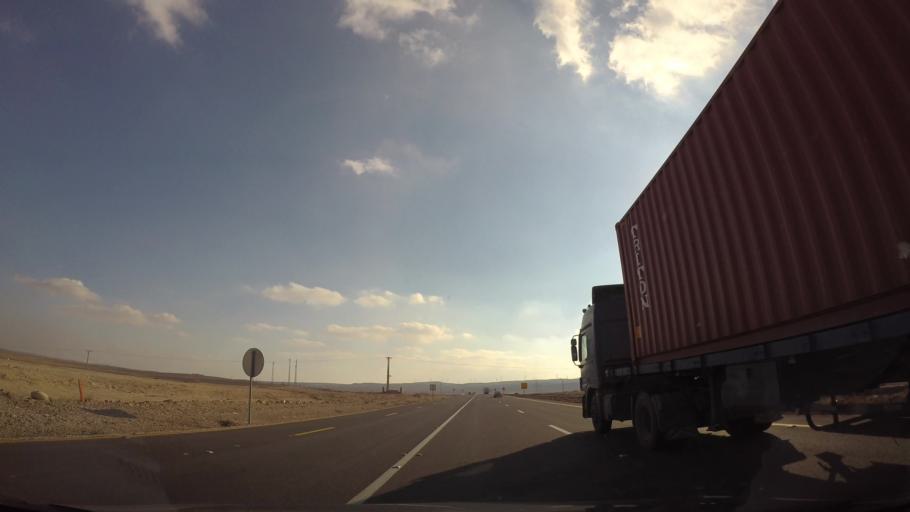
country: JO
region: Karak
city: Karak City
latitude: 31.1188
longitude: 36.0111
